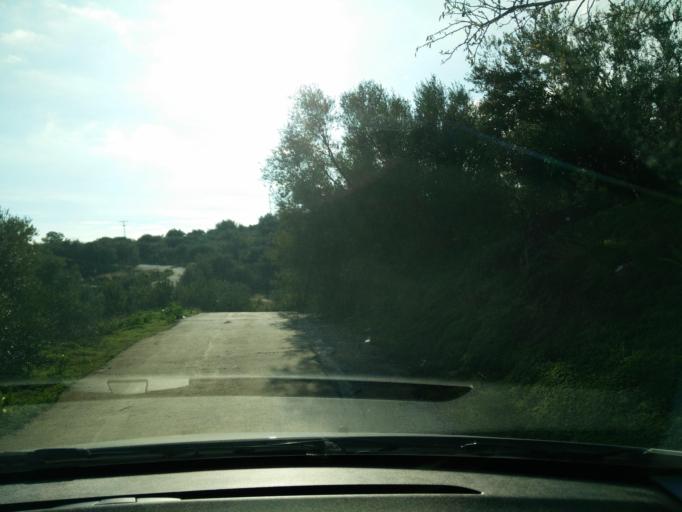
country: GR
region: Crete
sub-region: Nomos Lasithiou
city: Gra Liyia
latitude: 35.0273
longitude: 25.5688
